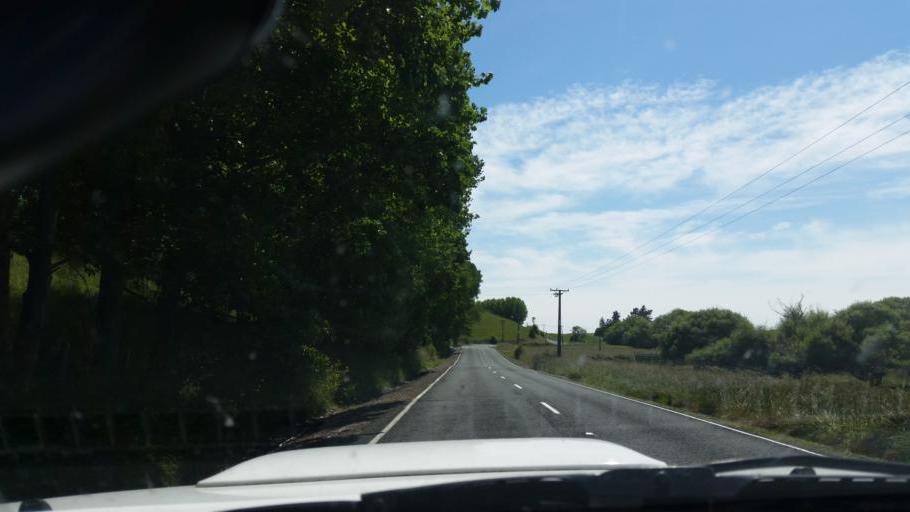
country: NZ
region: Auckland
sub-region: Auckland
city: Wellsford
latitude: -36.1917
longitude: 174.4032
